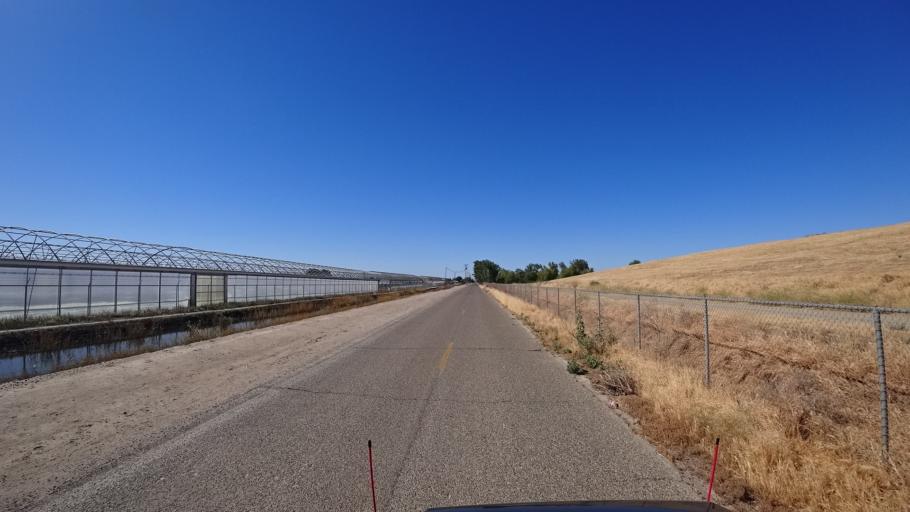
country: US
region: California
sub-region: Fresno County
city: West Park
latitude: 36.6957
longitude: -119.8270
